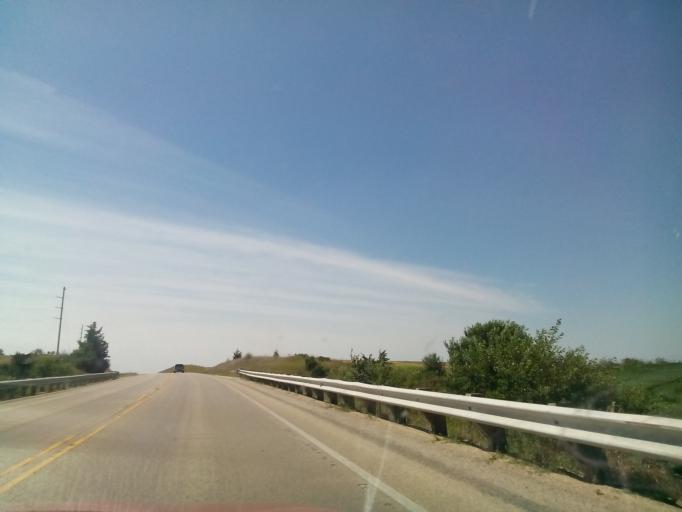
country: US
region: Wisconsin
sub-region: Green County
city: Monroe
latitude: 42.6548
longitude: -89.6296
